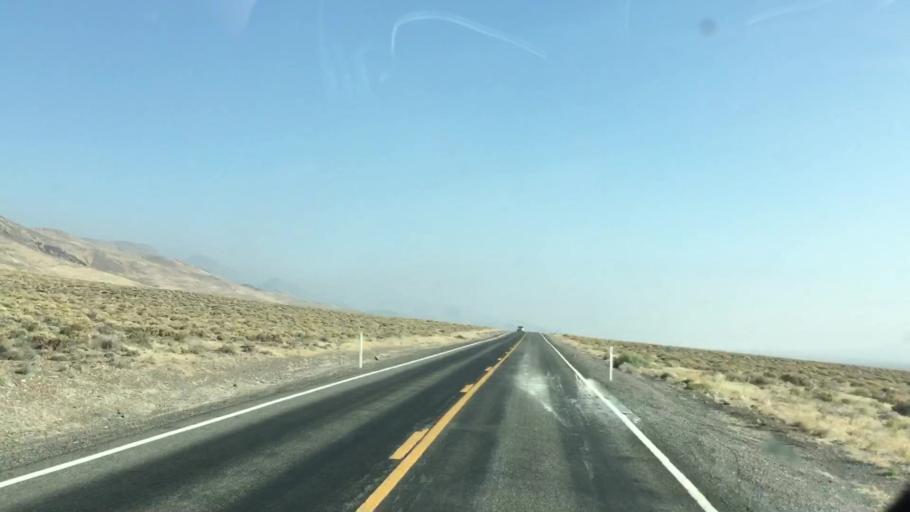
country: US
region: Nevada
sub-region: Lyon County
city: Fernley
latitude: 39.9495
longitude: -119.3855
